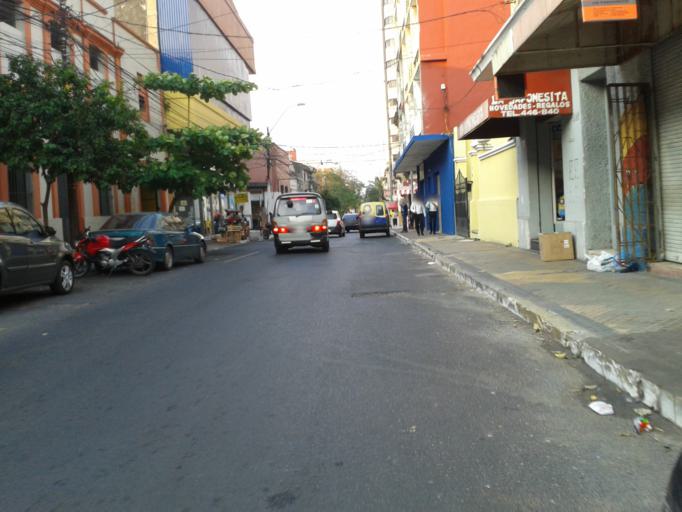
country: PY
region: Asuncion
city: Asuncion
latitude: -25.2861
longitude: -57.6379
